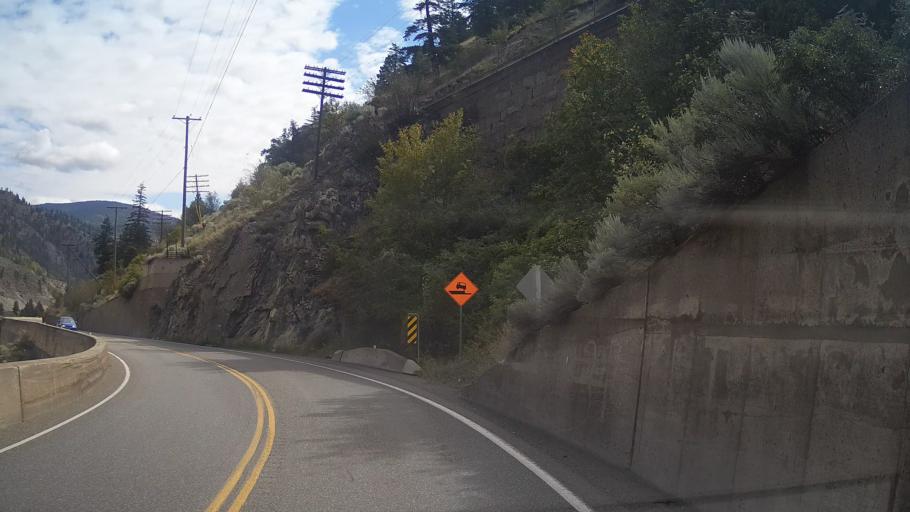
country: CA
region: British Columbia
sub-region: Thompson-Nicola Regional District
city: Ashcroft
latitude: 50.2566
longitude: -121.4362
